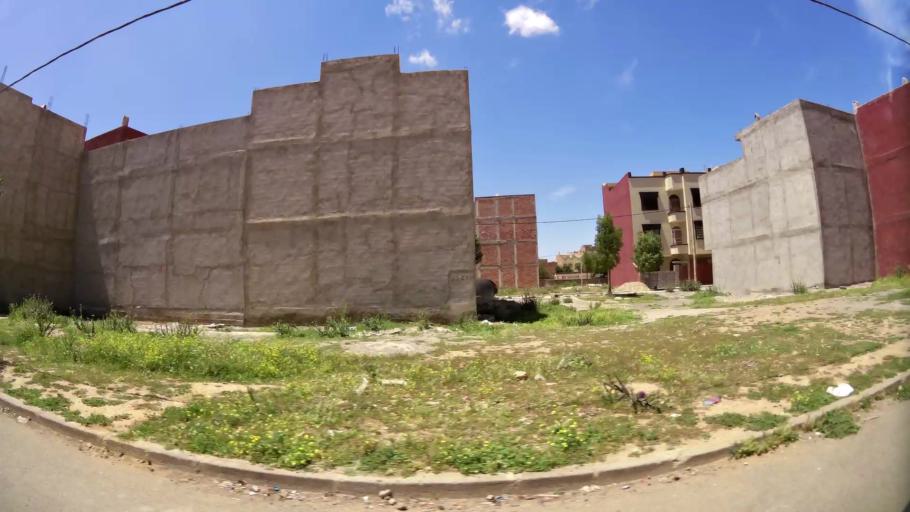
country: MA
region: Oriental
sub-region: Oujda-Angad
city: Oujda
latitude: 34.6637
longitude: -1.9399
